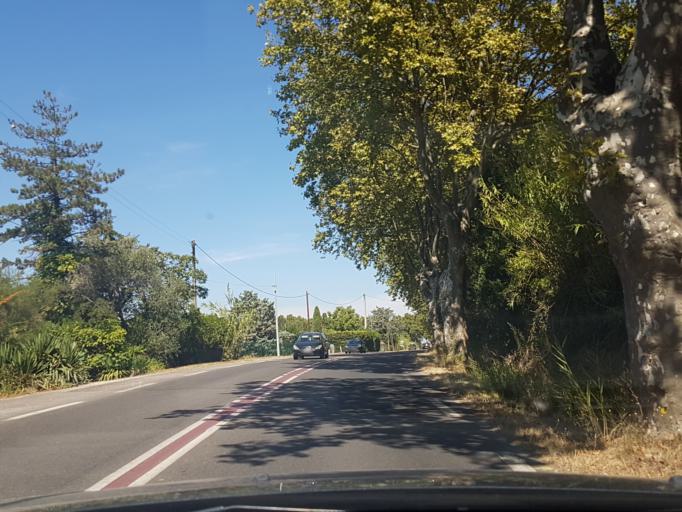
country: FR
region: Provence-Alpes-Cote d'Azur
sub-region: Departement des Bouches-du-Rhone
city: Saint-Remy-de-Provence
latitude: 43.8019
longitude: 4.8326
